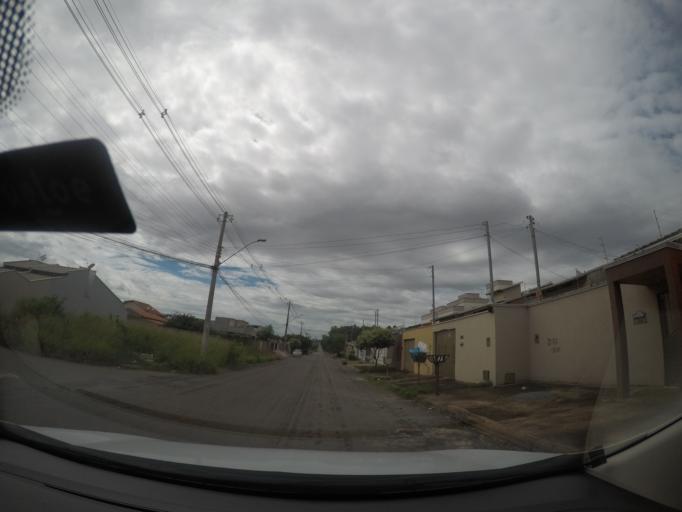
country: BR
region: Goias
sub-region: Goiania
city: Goiania
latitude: -16.7248
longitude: -49.3481
